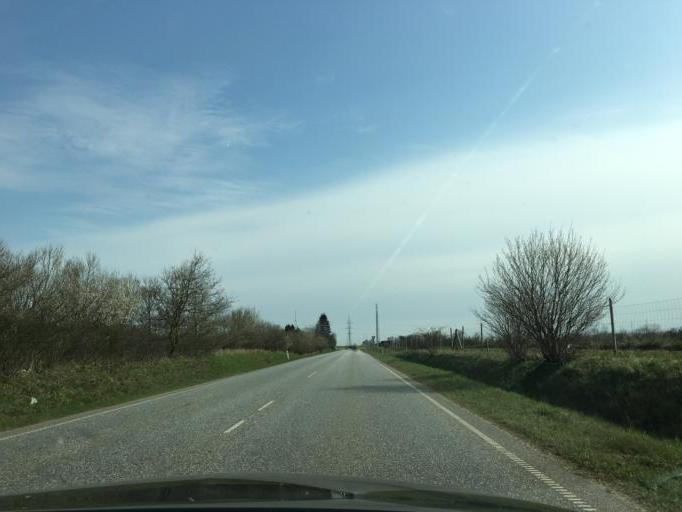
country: DK
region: South Denmark
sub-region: Kolding Kommune
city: Lunderskov
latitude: 55.5033
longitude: 9.3206
